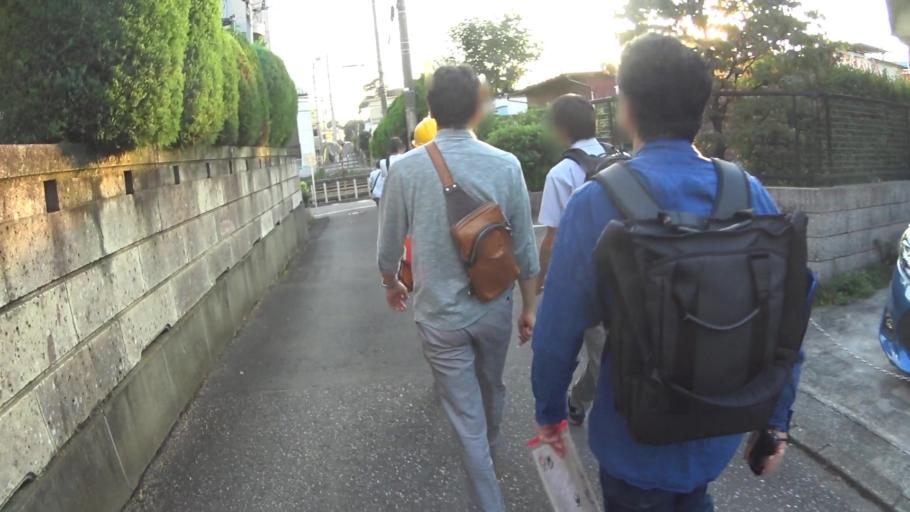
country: JP
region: Tokyo
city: Tanashicho
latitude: 35.7531
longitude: 139.5428
